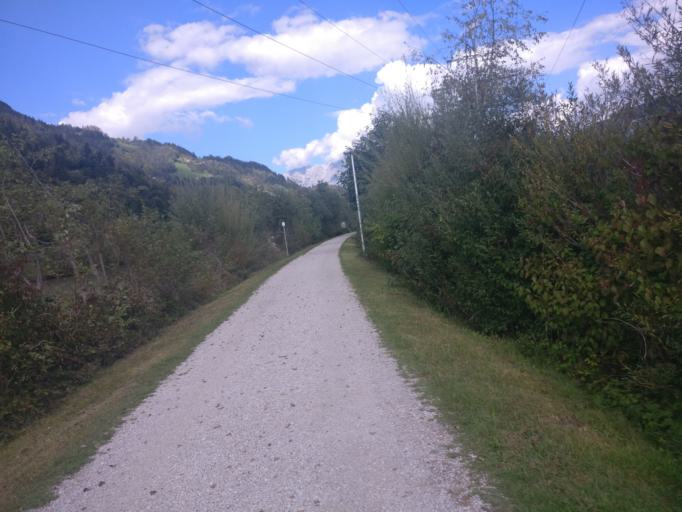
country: AT
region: Salzburg
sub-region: Politischer Bezirk Sankt Johann im Pongau
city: Sankt Johann im Pongau
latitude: 47.3717
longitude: 13.2102
